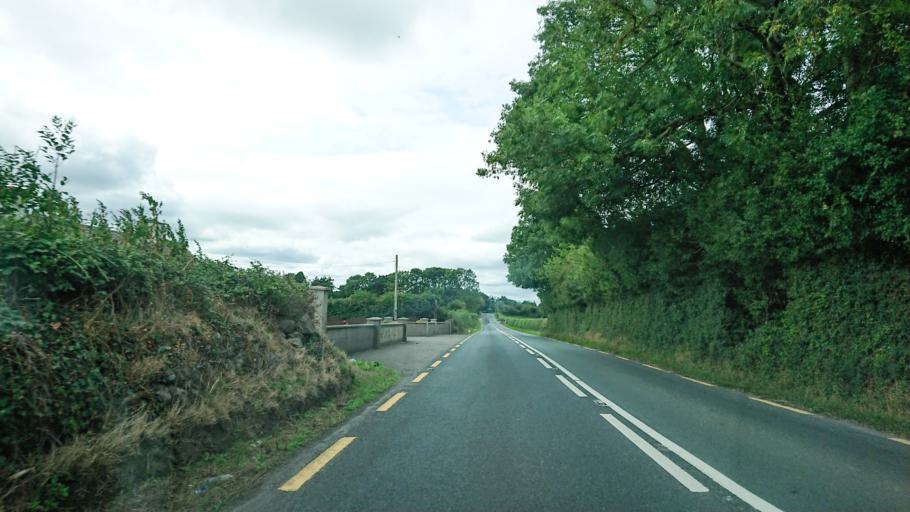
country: IE
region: Munster
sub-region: Waterford
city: Dungarvan
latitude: 52.1111
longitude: -7.6932
